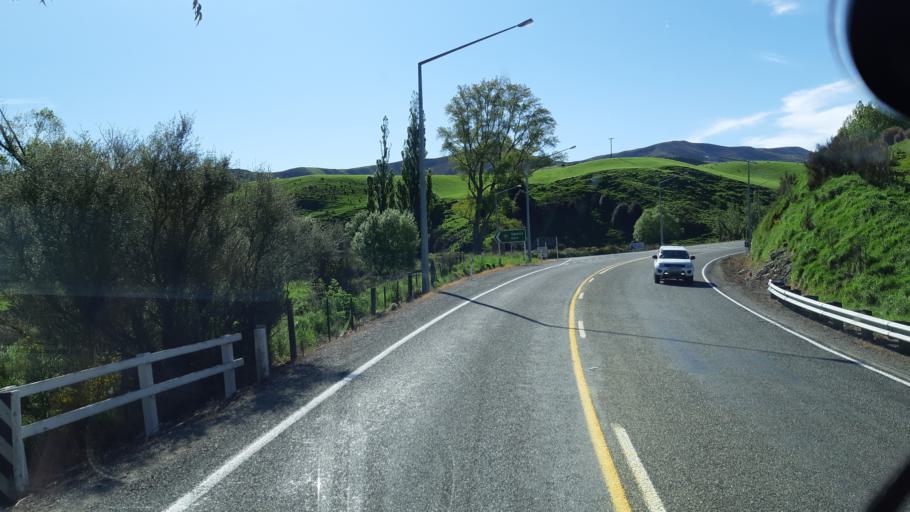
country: NZ
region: Otago
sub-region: Clutha District
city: Balclutha
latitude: -45.7864
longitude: 169.4686
